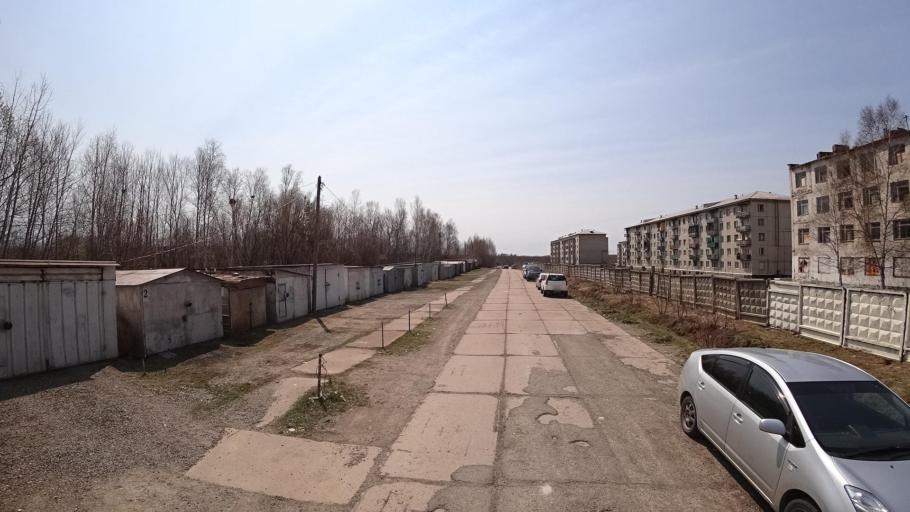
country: RU
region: Khabarovsk Krai
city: Selikhino
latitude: 50.3898
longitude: 137.3738
